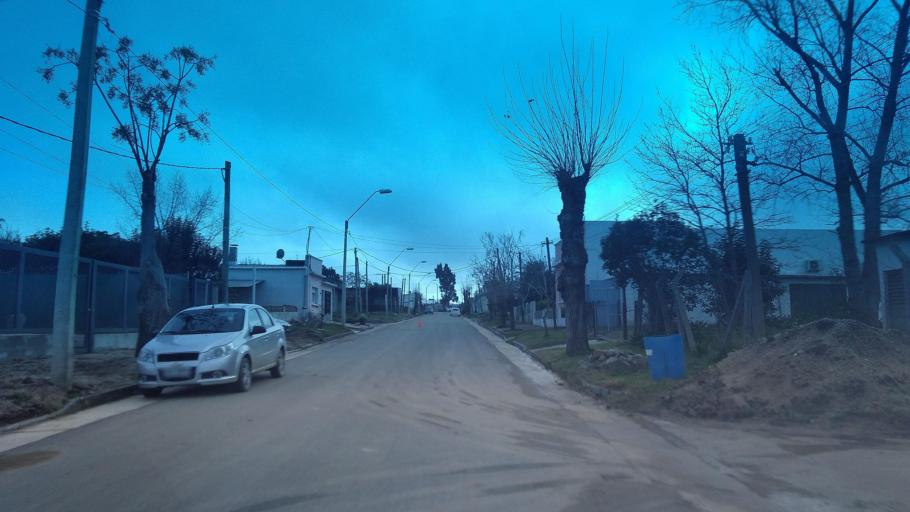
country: UY
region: Canelones
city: Tala
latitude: -34.1978
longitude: -55.7407
